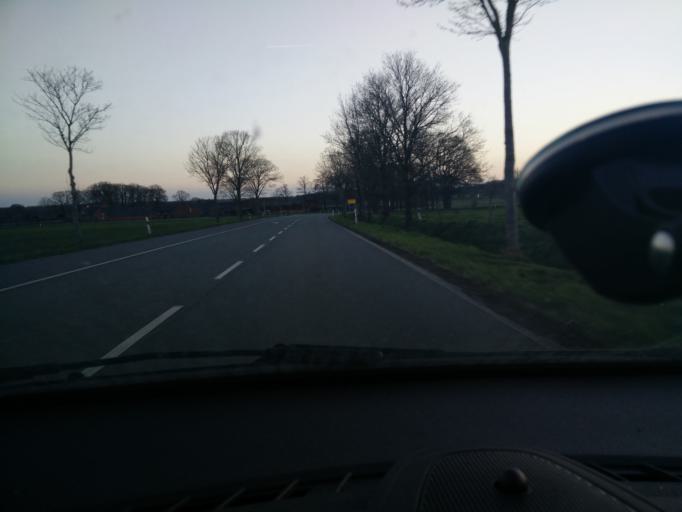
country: DE
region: North Rhine-Westphalia
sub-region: Regierungsbezirk Munster
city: Rhede
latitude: 51.7408
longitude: 6.7293
